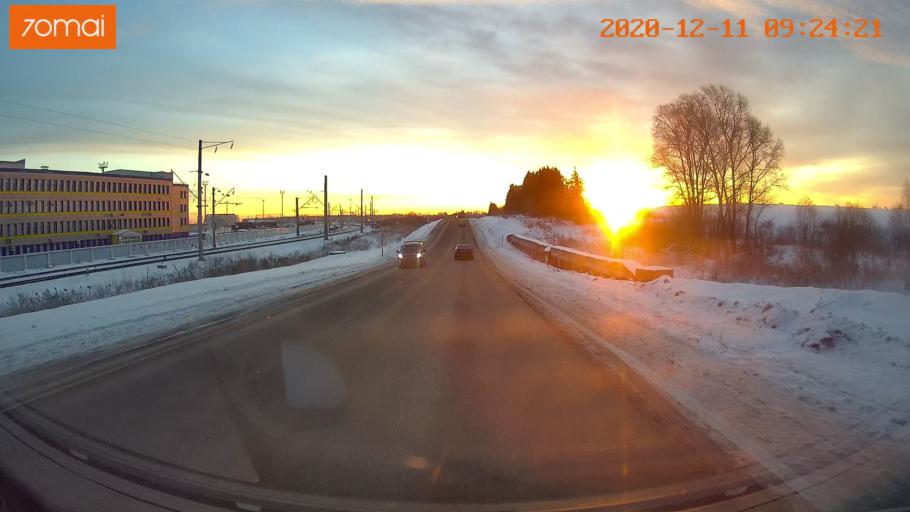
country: RU
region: Vologda
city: Vologda
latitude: 59.1808
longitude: 39.9610
